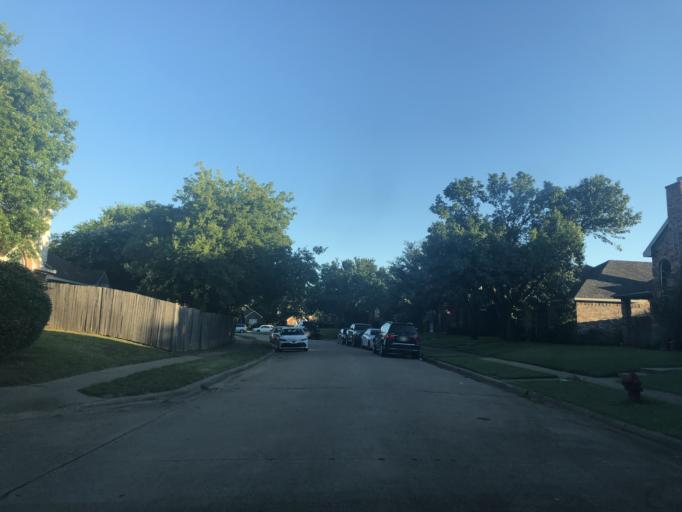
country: US
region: Texas
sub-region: Dallas County
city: Grand Prairie
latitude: 32.6675
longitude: -96.9942
